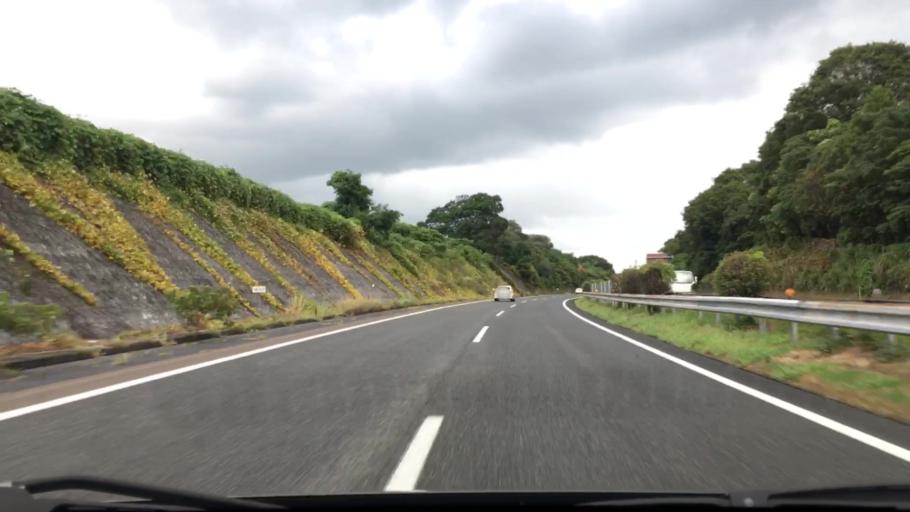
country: JP
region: Fukuoka
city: Miyata
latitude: 33.7473
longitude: 130.6137
